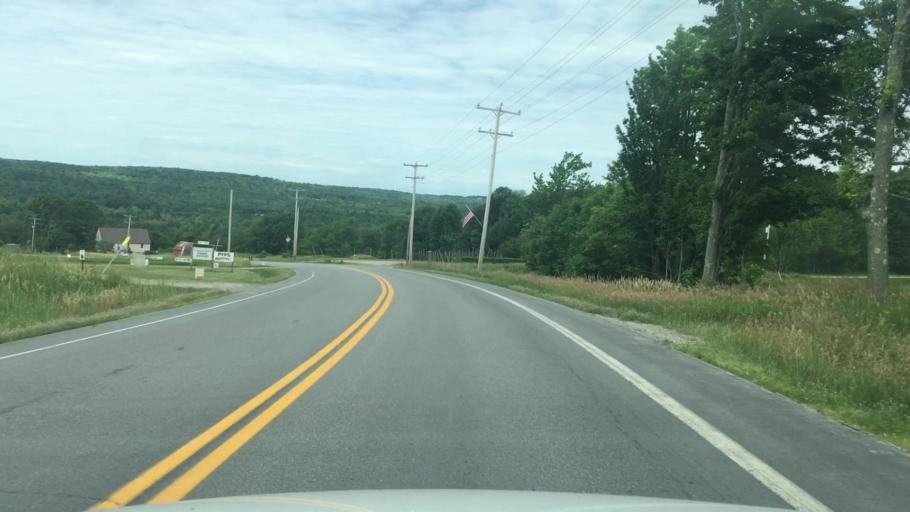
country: US
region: Maine
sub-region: Waldo County
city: Troy
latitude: 44.5343
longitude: -69.2739
